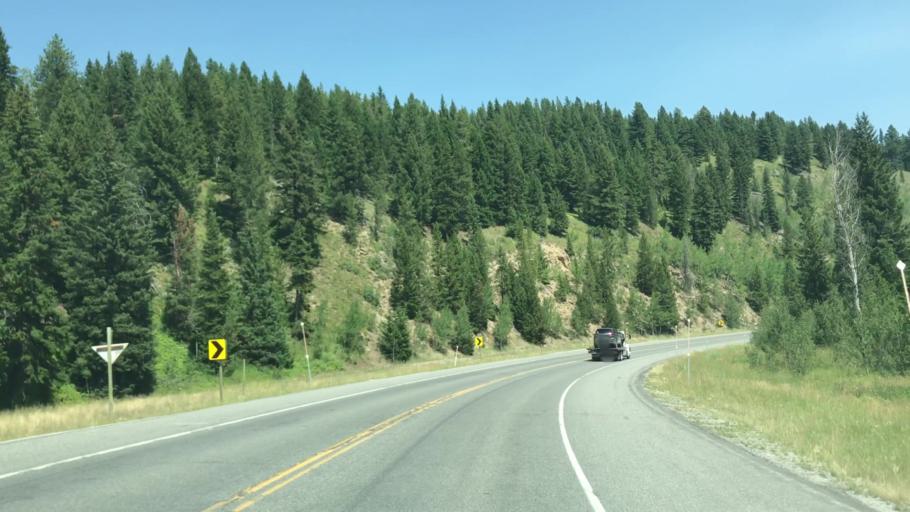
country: US
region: Montana
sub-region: Gallatin County
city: West Yellowstone
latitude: 44.8028
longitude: -111.1091
